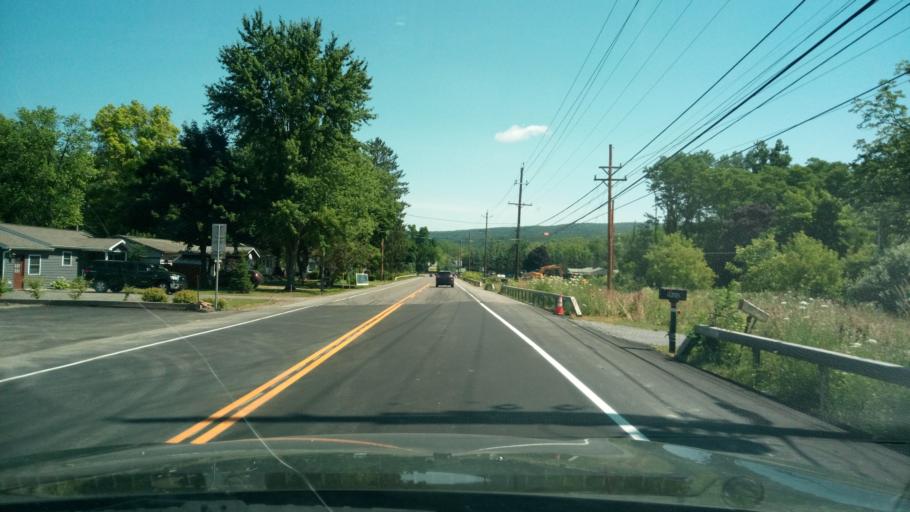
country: US
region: New York
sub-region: Schuyler County
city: Montour Falls
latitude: 42.3287
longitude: -76.8407
